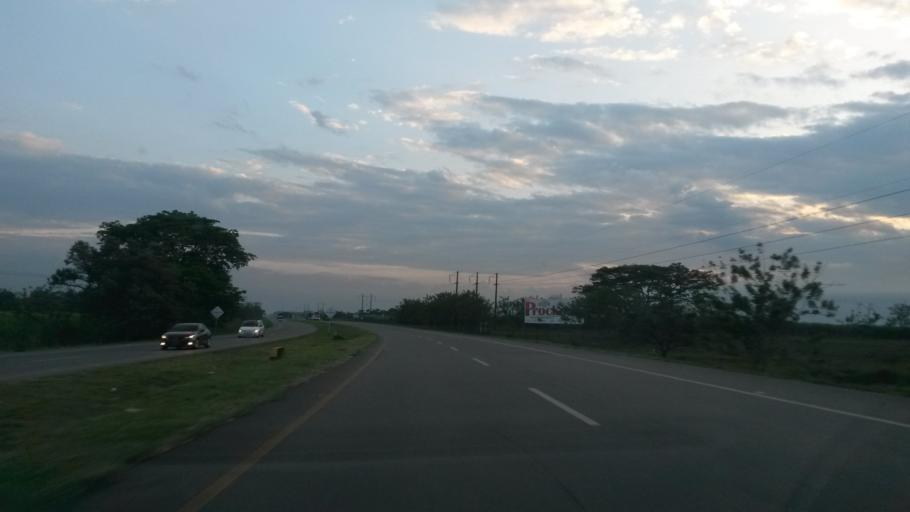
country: CO
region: Cauca
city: Santander de Quilichao
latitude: 3.0882
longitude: -76.4713
